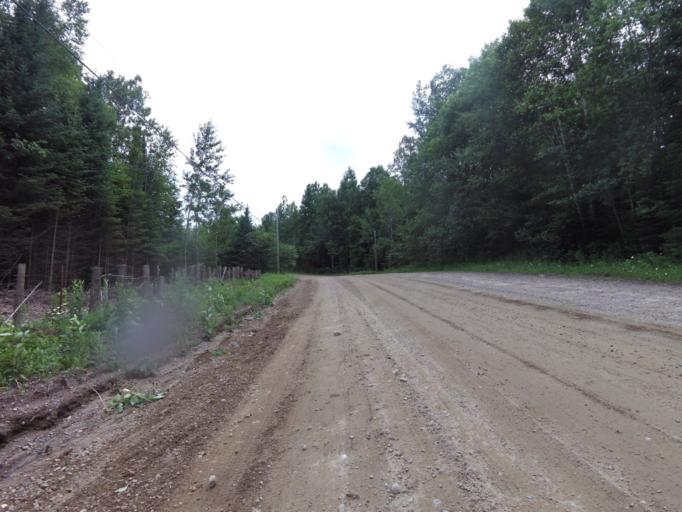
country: CA
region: Quebec
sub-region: Laurentides
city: Mont-Tremblant
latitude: 45.9422
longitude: -74.6483
